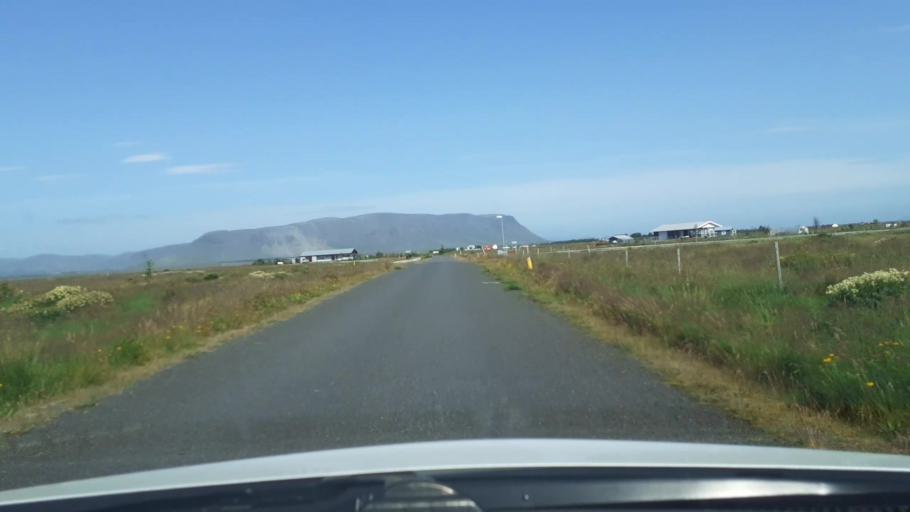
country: IS
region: South
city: Selfoss
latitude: 63.8978
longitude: -21.0822
